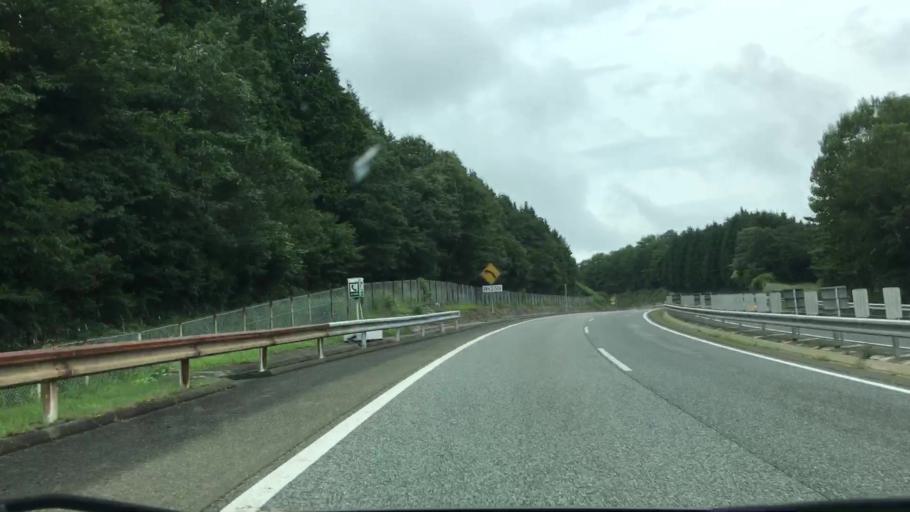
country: JP
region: Hiroshima
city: Shobara
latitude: 34.8720
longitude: 133.1454
